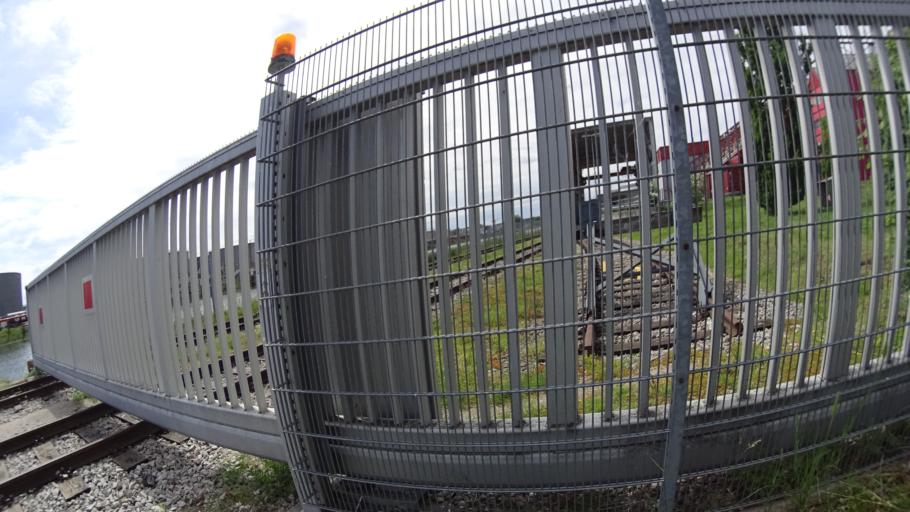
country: DE
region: Baden-Wuerttemberg
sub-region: Karlsruhe Region
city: Rheinstetten
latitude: 49.0131
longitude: 8.3220
